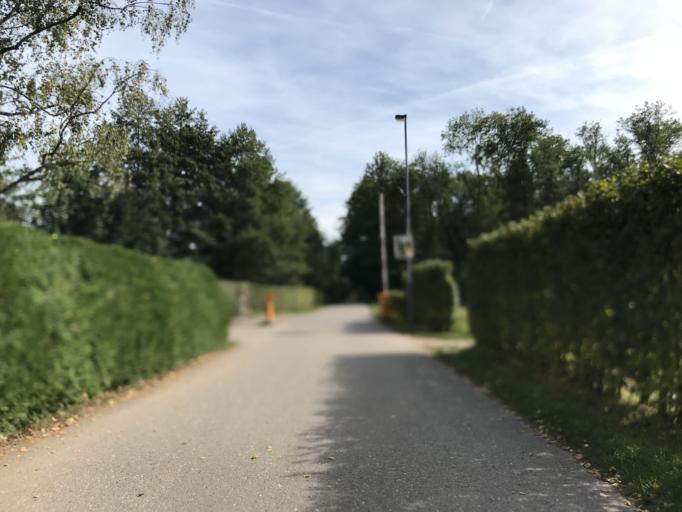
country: DE
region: Baden-Wuerttemberg
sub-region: Freiburg Region
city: Schopfheim
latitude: 47.6653
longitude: 7.8306
